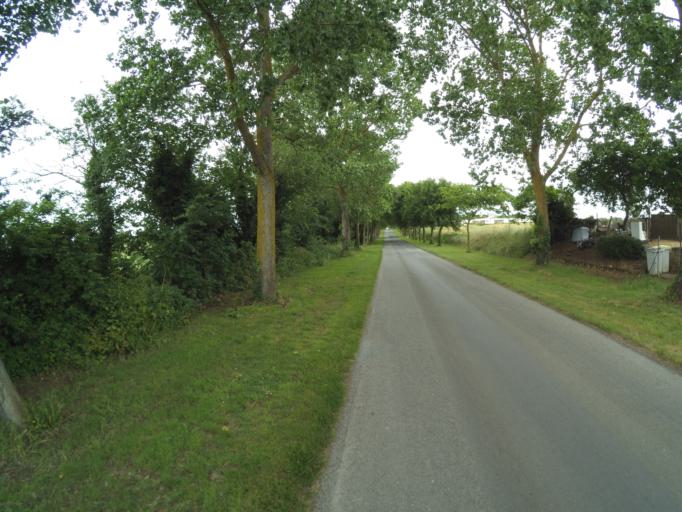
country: FR
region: Poitou-Charentes
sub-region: Departement de la Charente-Maritime
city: Saint-Laurent-de-la-Pree
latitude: 45.9879
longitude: -1.0145
